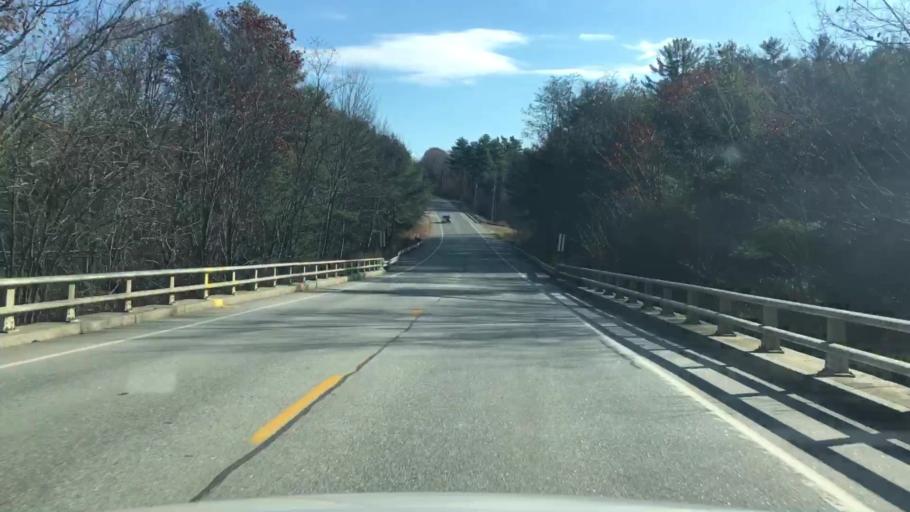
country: US
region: Maine
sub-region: Kennebec County
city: Windsor
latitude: 44.2583
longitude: -69.5539
